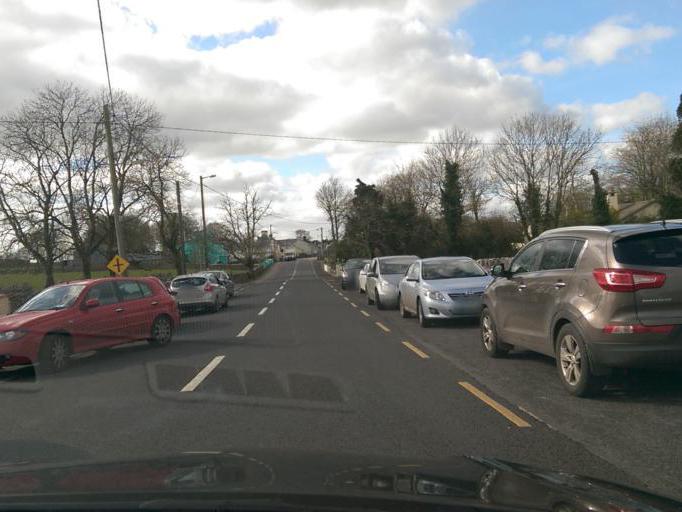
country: IE
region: Connaught
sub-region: County Galway
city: Athenry
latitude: 53.4213
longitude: -8.5696
